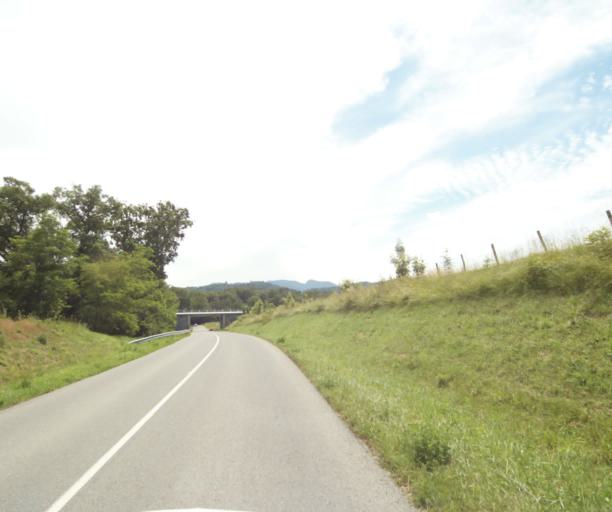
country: FR
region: Rhone-Alpes
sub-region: Departement de la Haute-Savoie
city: Allinges
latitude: 46.3480
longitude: 6.4521
